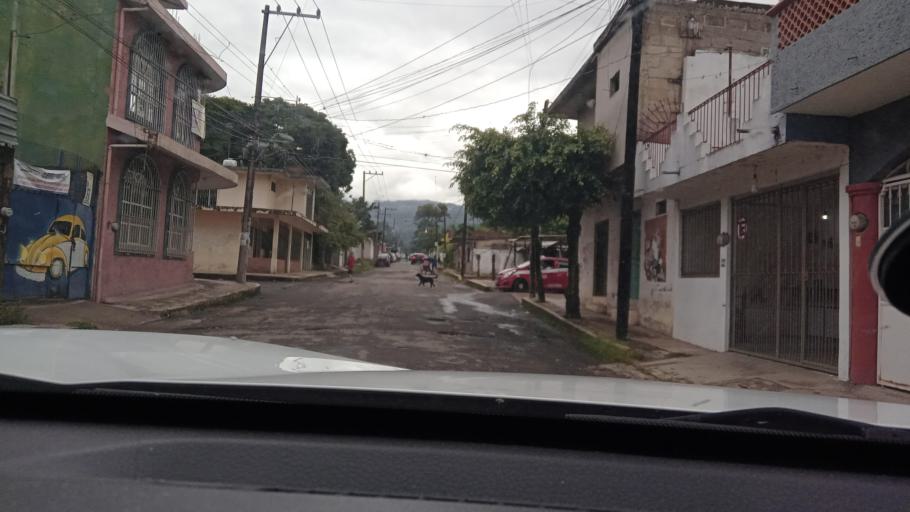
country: MX
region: Veracruz
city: Coatepec
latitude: 19.4480
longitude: -96.9698
